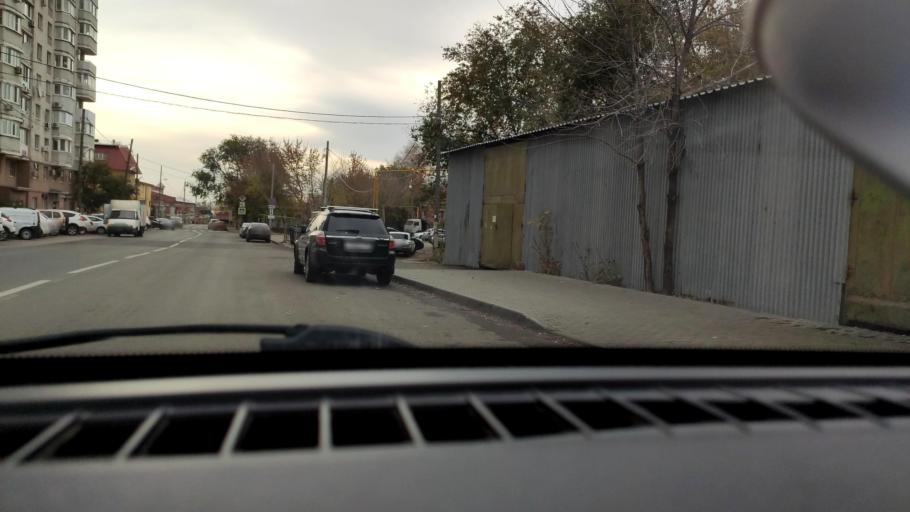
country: RU
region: Samara
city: Samara
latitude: 53.1814
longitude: 50.0929
